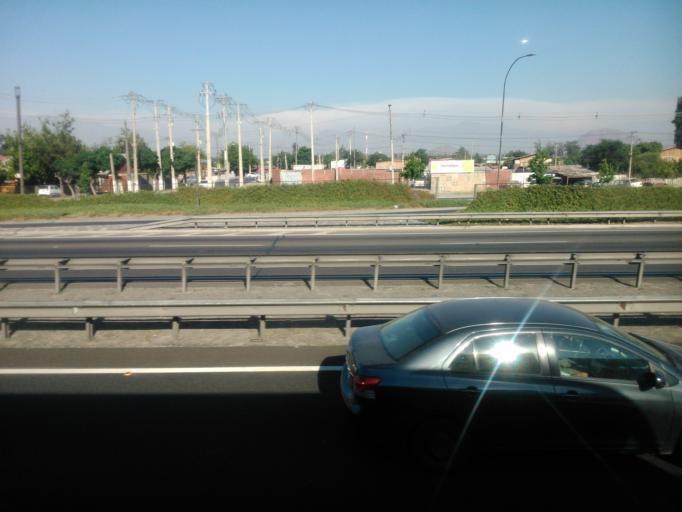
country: CL
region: Santiago Metropolitan
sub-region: Provincia de Maipo
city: San Bernardo
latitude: -33.6041
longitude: -70.7167
